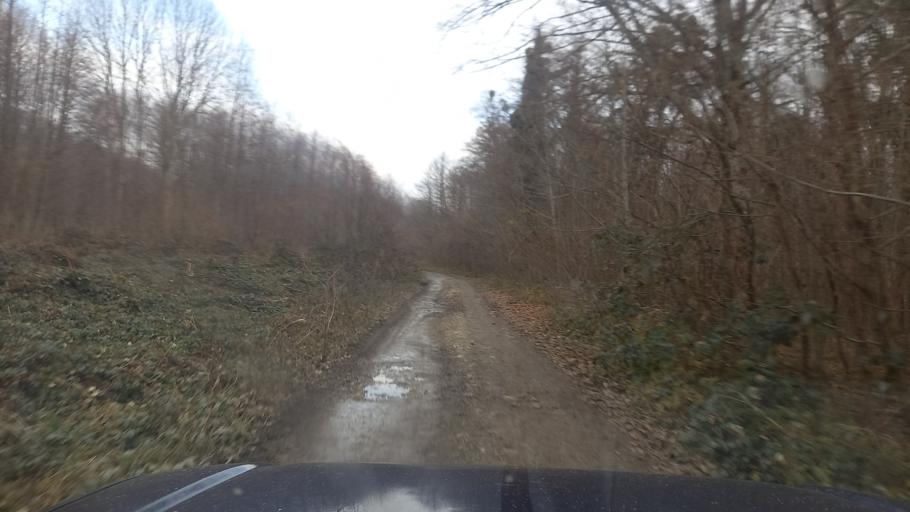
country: RU
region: Krasnodarskiy
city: Neftegorsk
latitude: 44.2223
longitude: 39.7339
